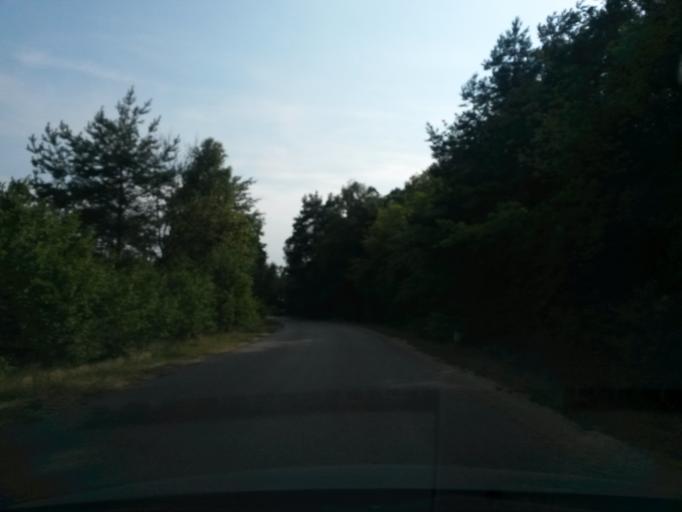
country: PL
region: Kujawsko-Pomorskie
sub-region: Powiat rypinski
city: Skrwilno
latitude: 52.9726
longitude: 19.6285
